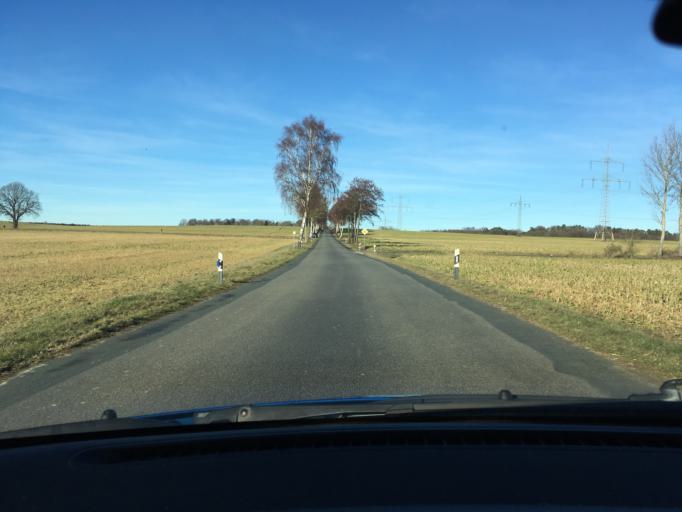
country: DE
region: Lower Saxony
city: Hanstedt Eins
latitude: 53.0623
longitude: 10.3843
